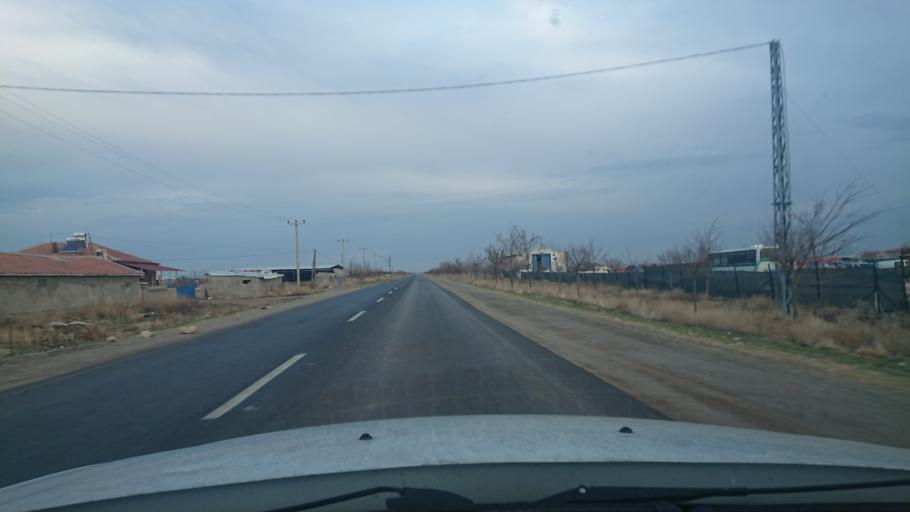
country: TR
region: Aksaray
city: Yesilova
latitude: 38.2973
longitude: 33.7583
